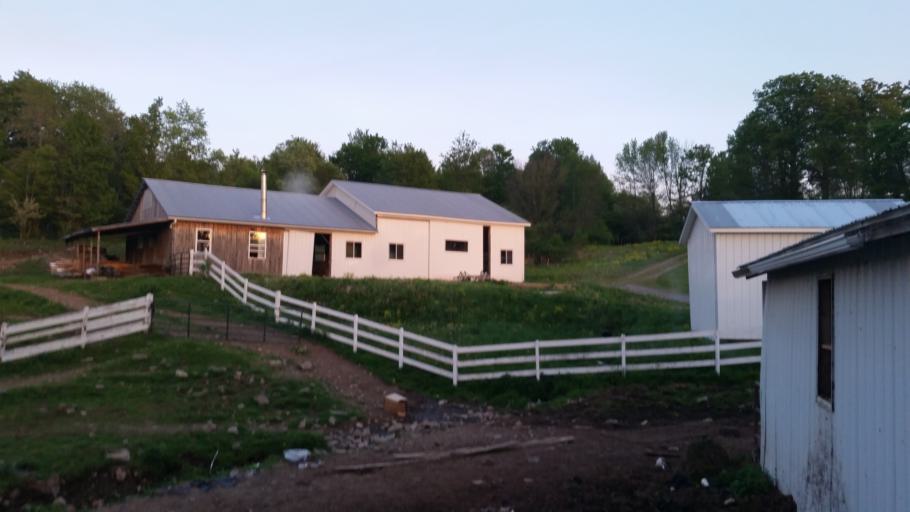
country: US
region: New York
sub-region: Allegany County
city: Andover
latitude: 41.9470
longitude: -77.7684
